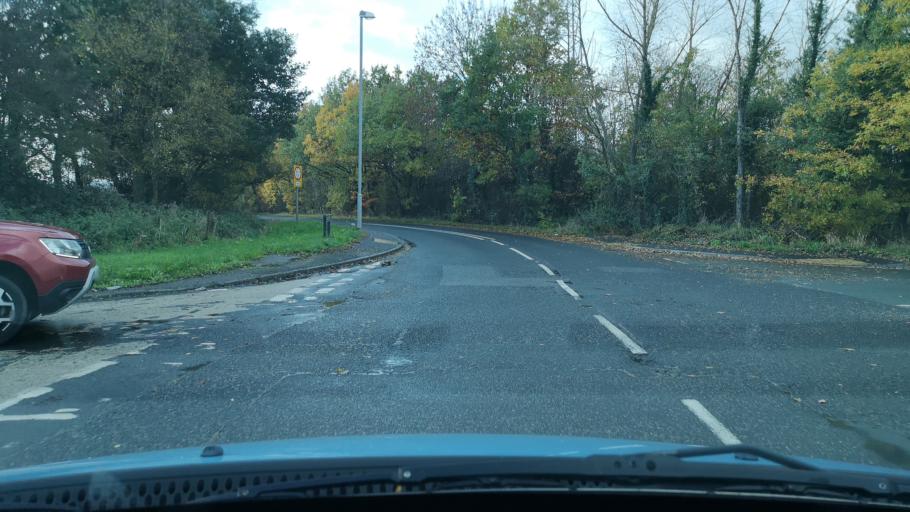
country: GB
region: England
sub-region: City and Borough of Wakefield
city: Ryhill
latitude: 53.6137
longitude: -1.4268
